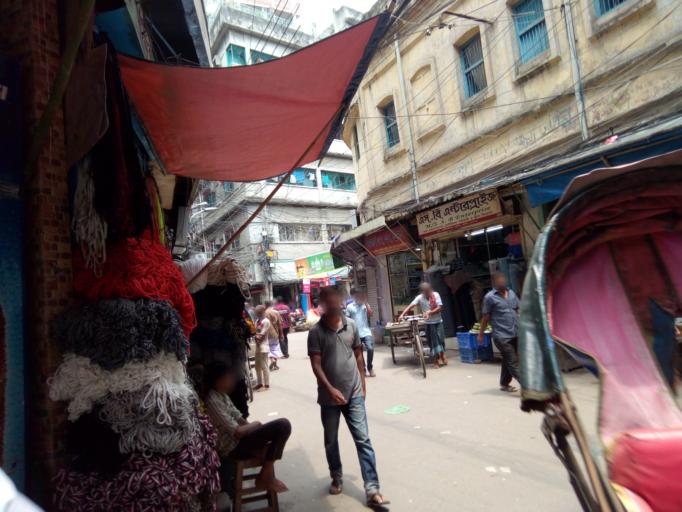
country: BD
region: Dhaka
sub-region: Dhaka
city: Dhaka
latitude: 23.7168
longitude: 90.4095
